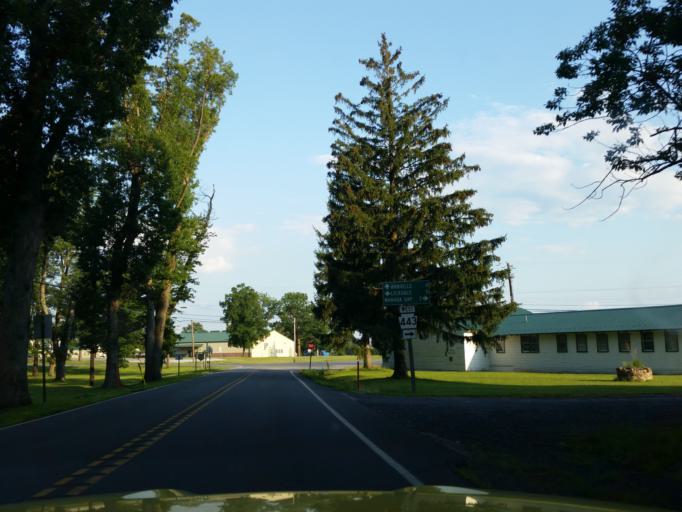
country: US
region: Pennsylvania
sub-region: Lebanon County
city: Jonestown
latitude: 40.4326
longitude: -76.5924
